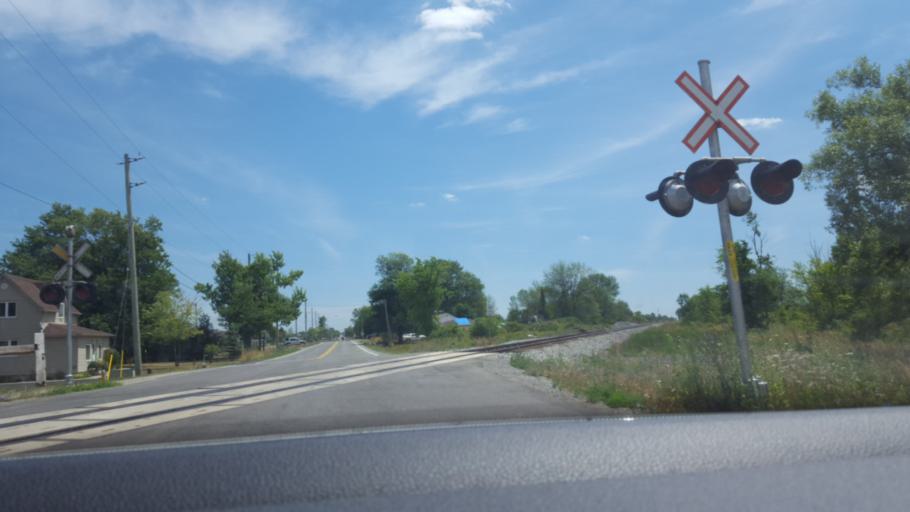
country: CA
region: Ontario
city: Hamilton
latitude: 43.1569
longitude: -79.6218
